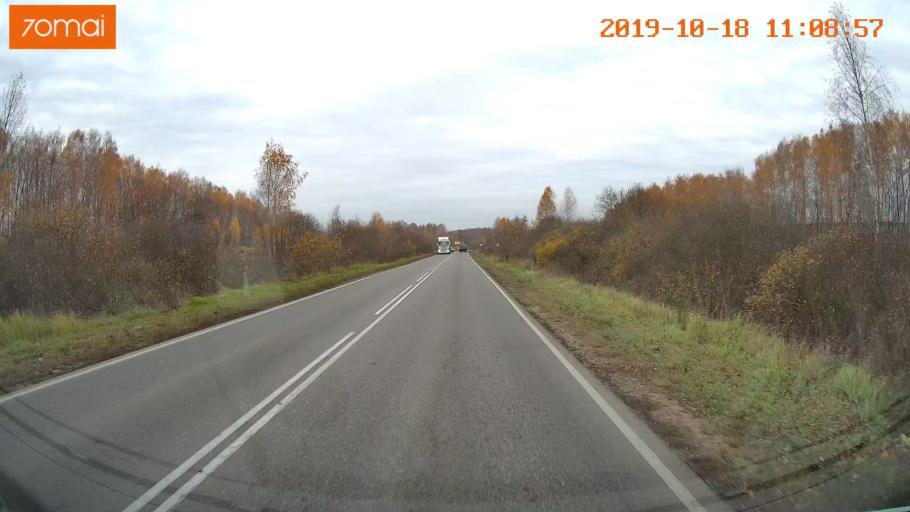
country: RU
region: Tula
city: Kimovsk
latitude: 53.9462
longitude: 38.5337
